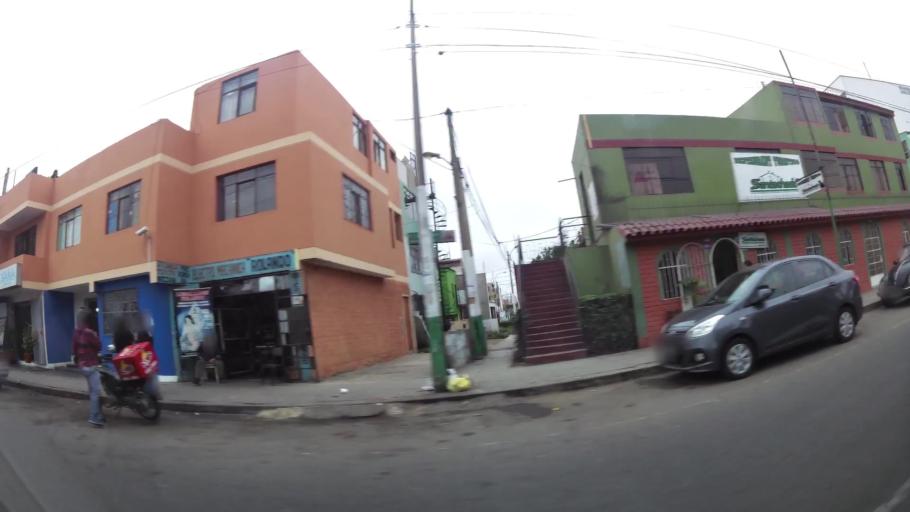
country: PE
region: Callao
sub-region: Callao
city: Callao
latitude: -12.0654
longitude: -77.1043
